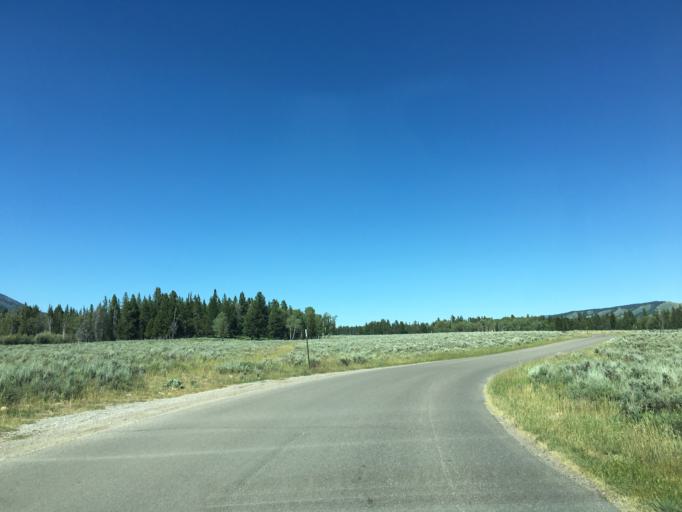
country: US
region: Wyoming
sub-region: Teton County
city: Moose Wilson Road
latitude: 43.6009
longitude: -110.7971
